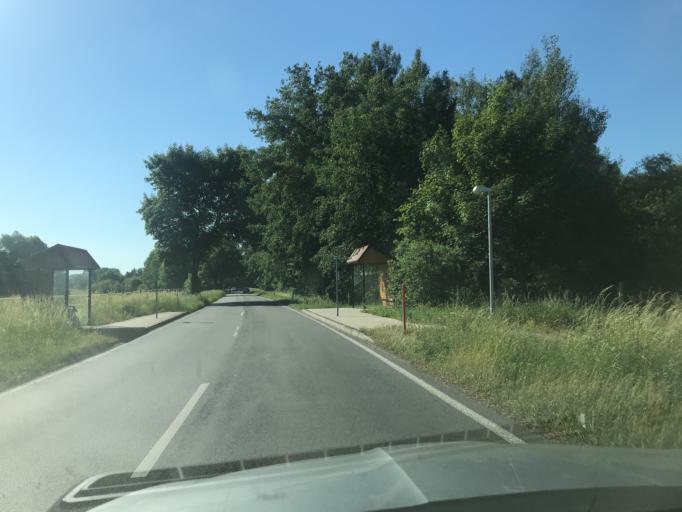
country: DE
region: Brandenburg
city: Bernau bei Berlin
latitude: 52.6460
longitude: 13.6080
